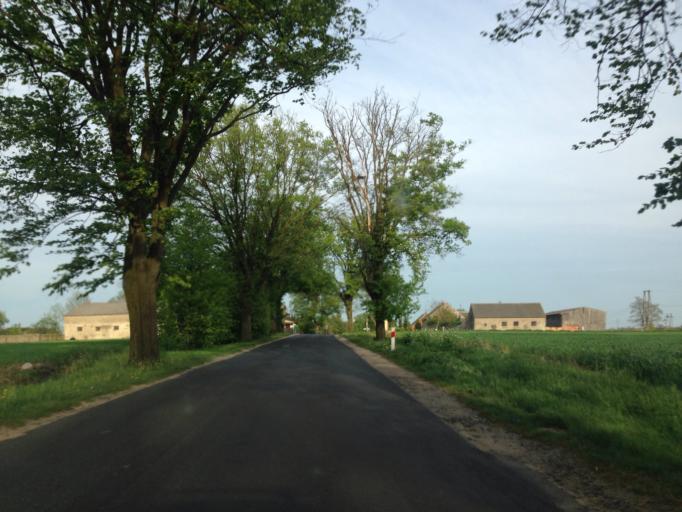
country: PL
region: Kujawsko-Pomorskie
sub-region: Powiat wabrzeski
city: Debowa Laka
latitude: 53.2388
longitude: 19.1529
